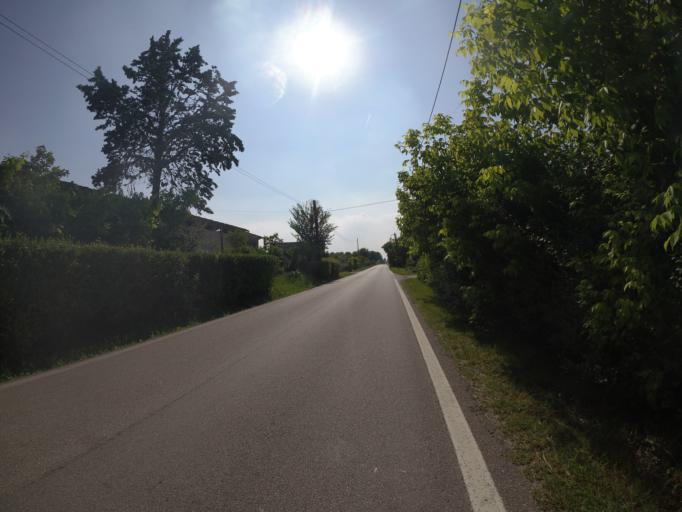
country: IT
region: Friuli Venezia Giulia
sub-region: Provincia di Udine
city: Varmo
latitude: 45.9192
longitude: 12.9908
